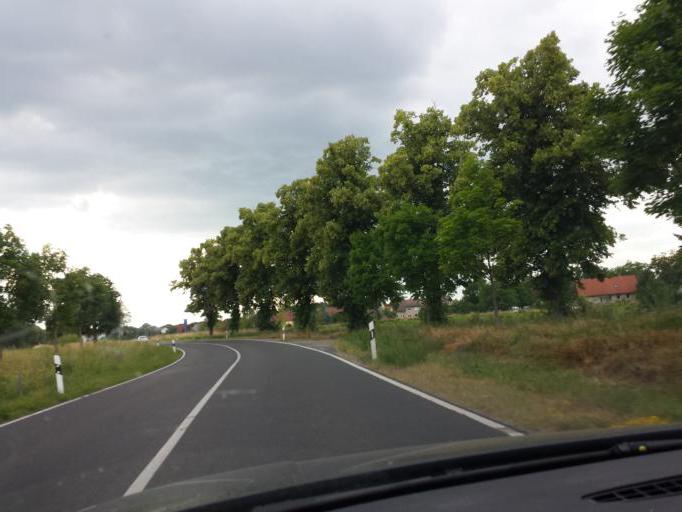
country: DE
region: Brandenburg
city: Mittenwalde
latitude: 52.3057
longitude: 13.5127
